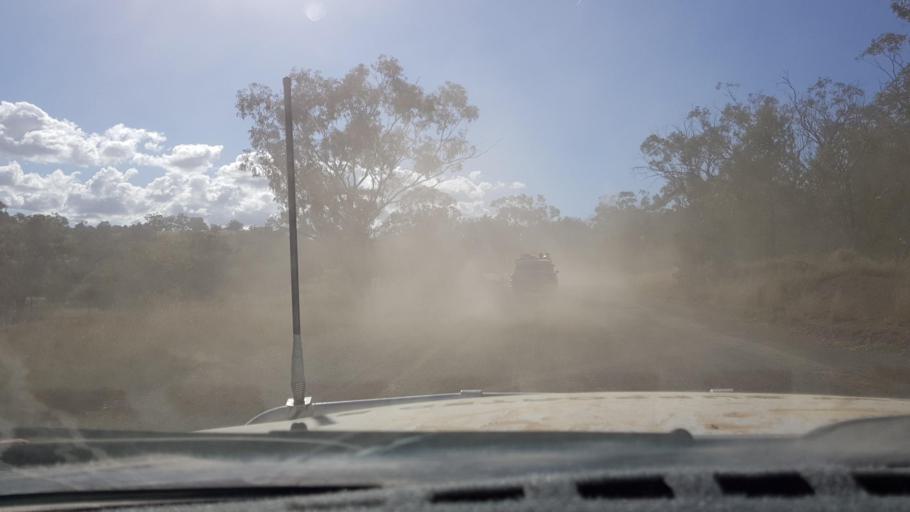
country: AU
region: New South Wales
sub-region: Tamworth Municipality
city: Manilla
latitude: -30.6580
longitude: 150.4834
